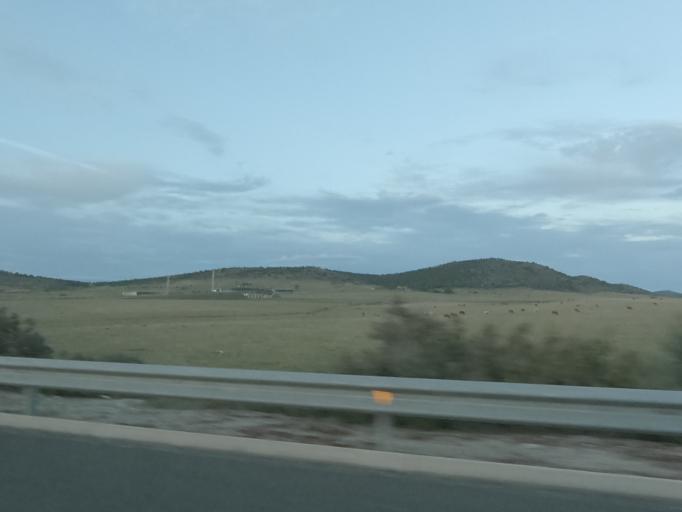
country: ES
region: Extremadura
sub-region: Provincia de Caceres
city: Caceres
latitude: 39.4107
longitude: -6.4015
